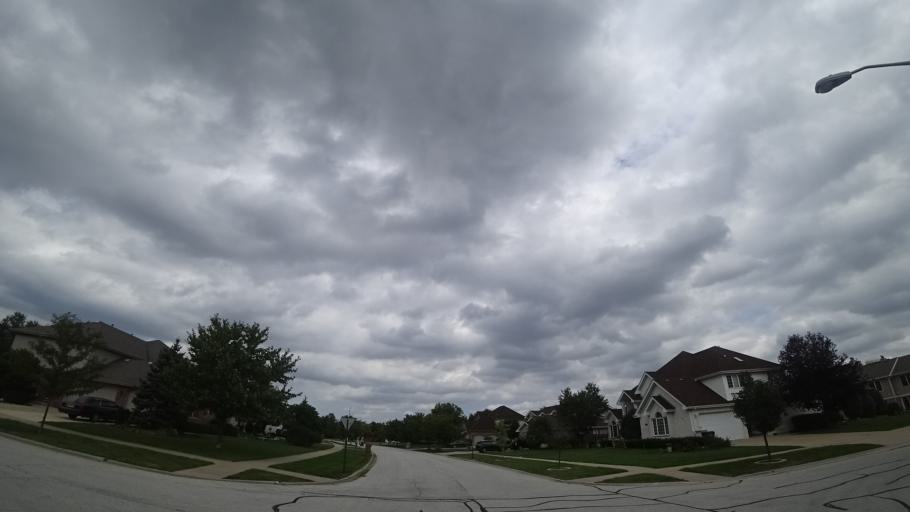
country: US
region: Illinois
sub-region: Cook County
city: Tinley Park
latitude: 41.5684
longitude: -87.8061
